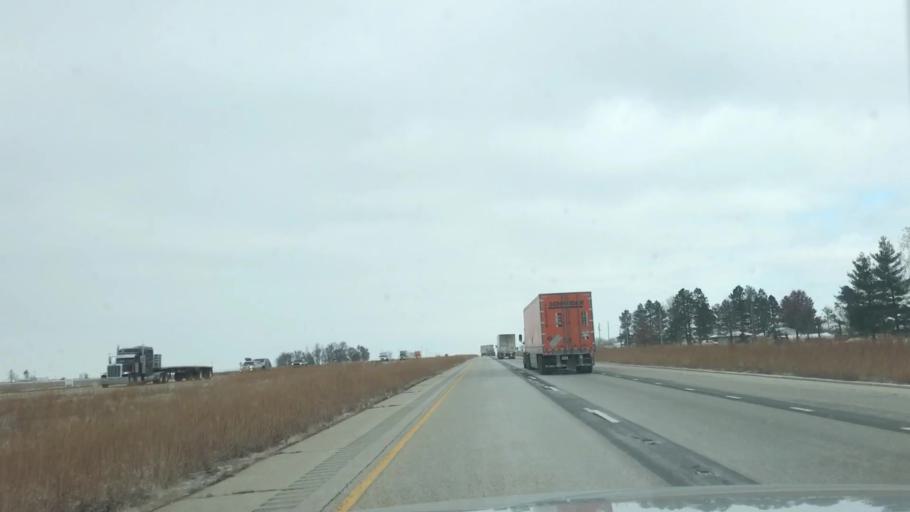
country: US
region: Illinois
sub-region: Sangamon County
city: Divernon
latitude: 39.4509
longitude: -89.6440
